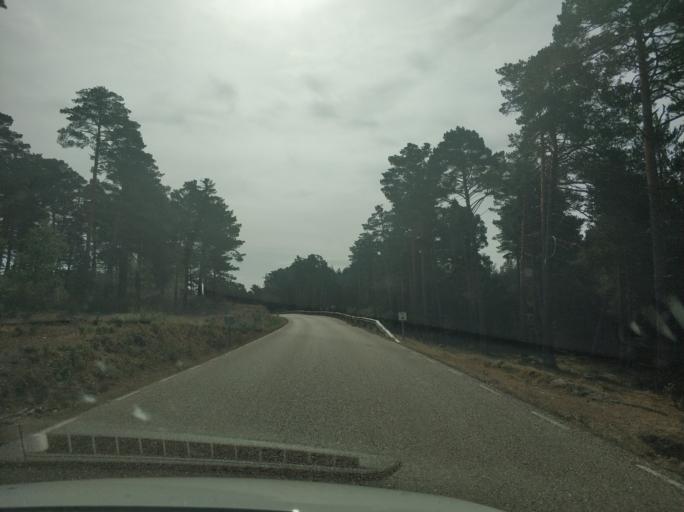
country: ES
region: Castille and Leon
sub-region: Provincia de Soria
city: Navaleno
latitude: 41.8547
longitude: -2.9658
